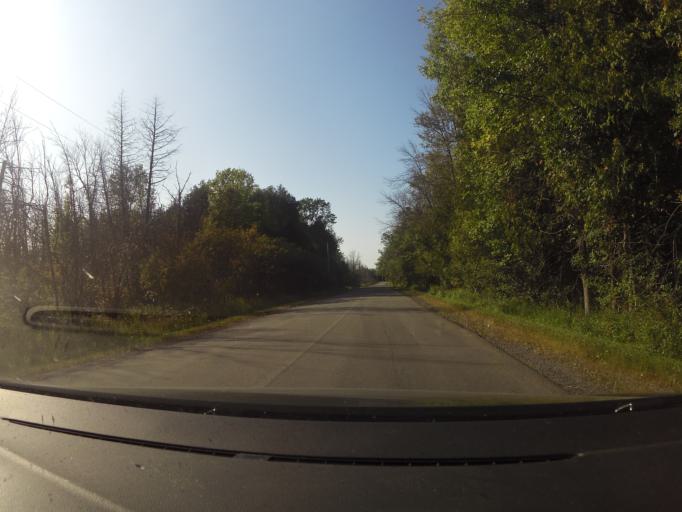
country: CA
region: Ontario
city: Carleton Place
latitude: 45.2895
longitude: -76.0837
